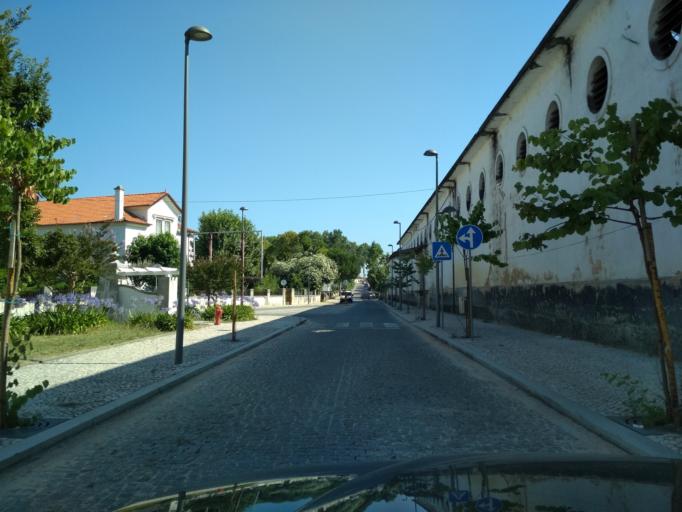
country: PT
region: Aveiro
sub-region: Mealhada
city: Mealhada
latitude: 40.3730
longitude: -8.4534
